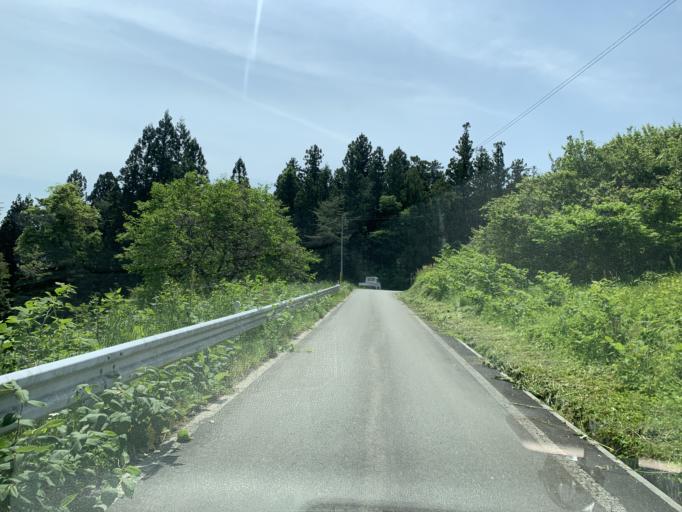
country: JP
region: Iwate
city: Ichinoseki
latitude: 38.9600
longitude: 141.2418
